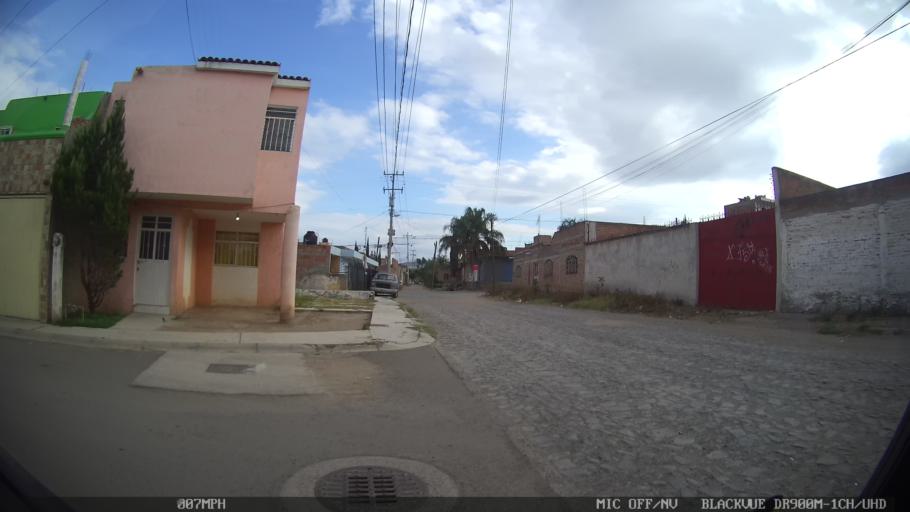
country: MX
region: Jalisco
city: Tonala
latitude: 20.6684
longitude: -103.2384
